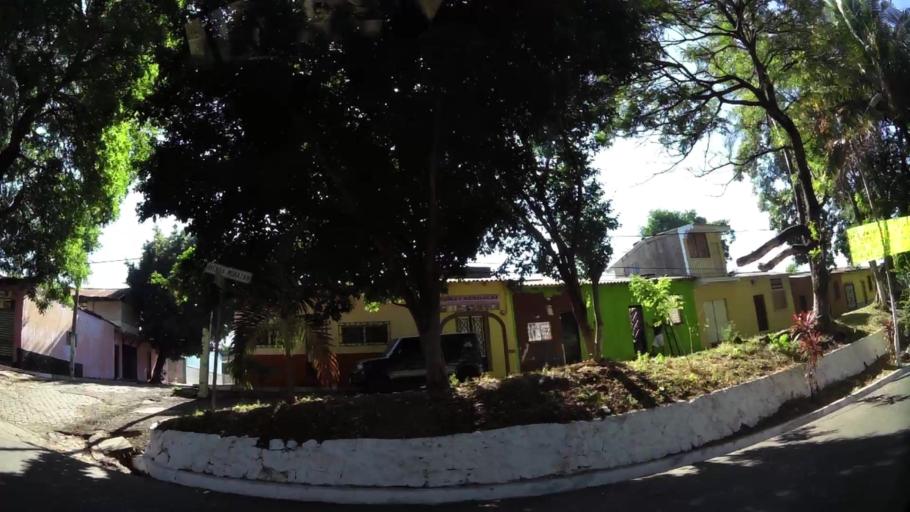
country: SV
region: Sonsonate
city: Sonsonate
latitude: 13.7271
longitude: -89.7228
